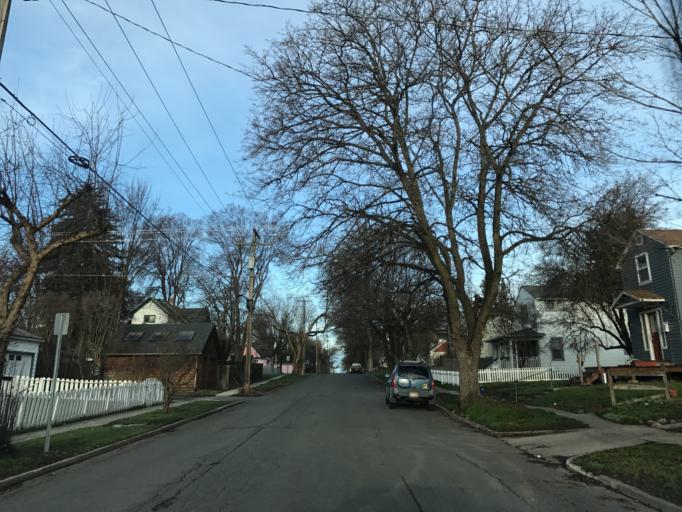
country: US
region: Idaho
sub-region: Latah County
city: Moscow
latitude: 46.7347
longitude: -116.9915
